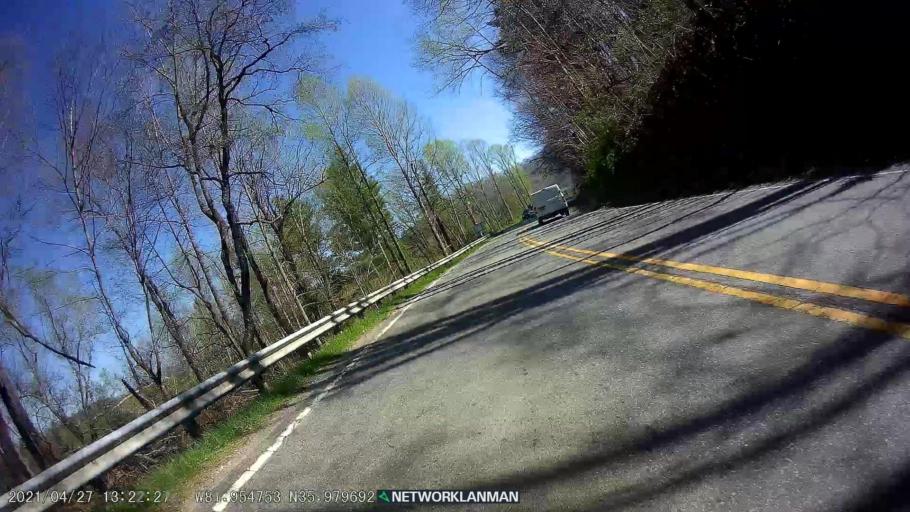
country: US
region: North Carolina
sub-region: Avery County
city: Newland
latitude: 35.9798
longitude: -81.9547
